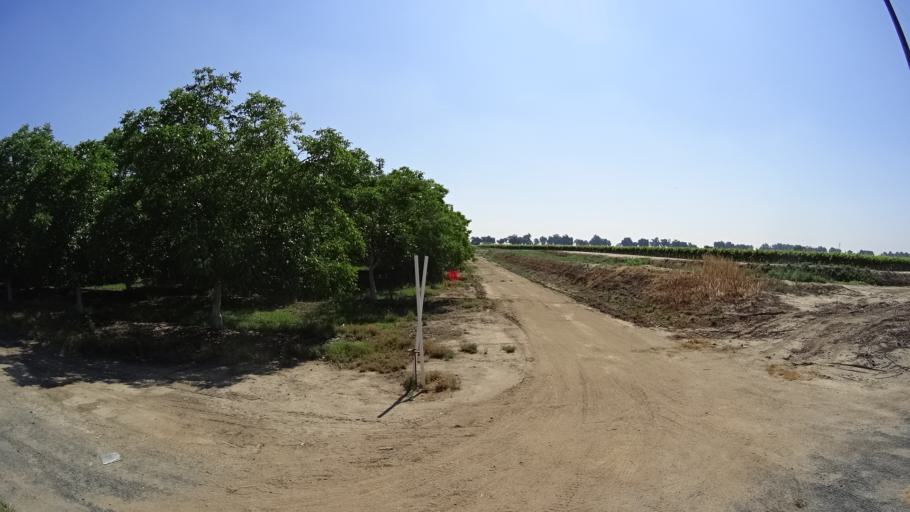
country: US
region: California
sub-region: Fresno County
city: Kingsburg
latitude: 36.4722
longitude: -119.5508
